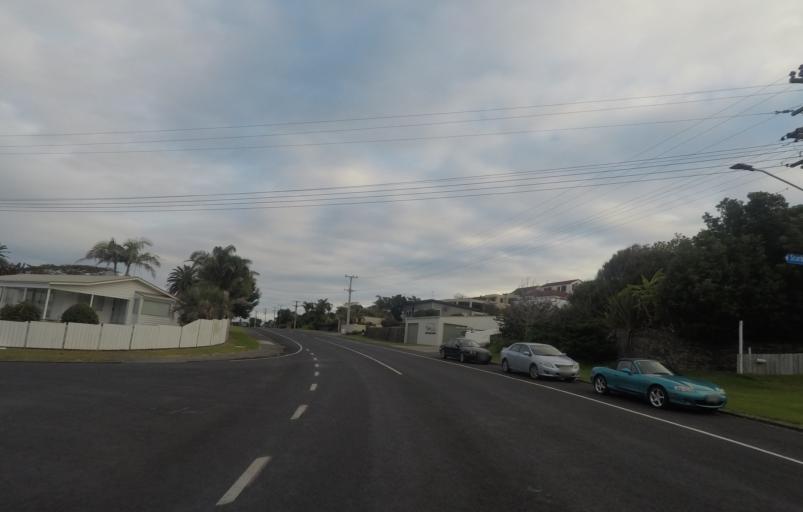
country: NZ
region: Bay of Plenty
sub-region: Western Bay of Plenty District
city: Waihi Beach
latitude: -37.4012
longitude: 175.9363
